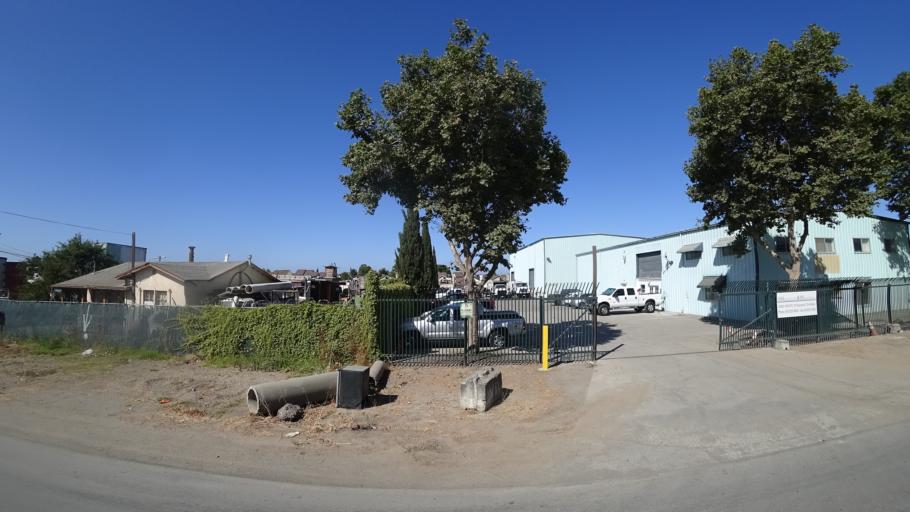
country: US
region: California
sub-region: Alameda County
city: Union City
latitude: 37.6275
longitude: -122.0537
